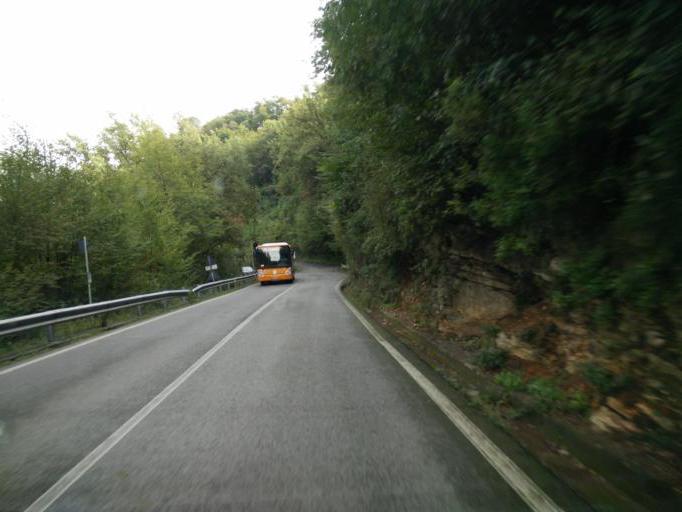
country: IT
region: Liguria
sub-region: Provincia di La Spezia
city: Le Grazie
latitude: 44.0729
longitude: 9.8348
